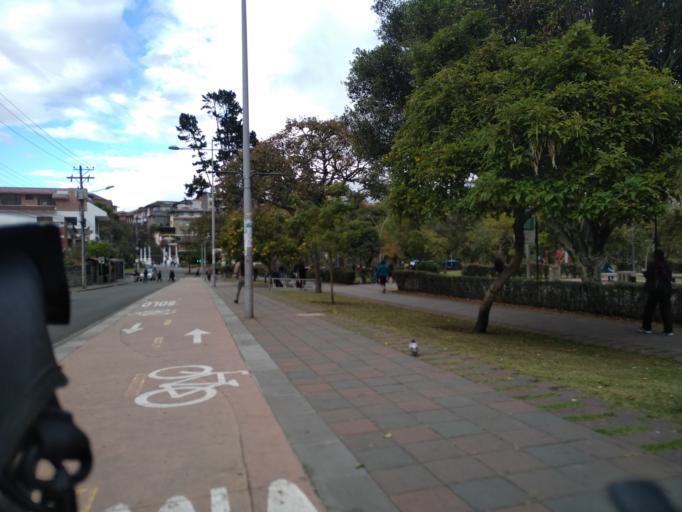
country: EC
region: Azuay
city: Cuenca
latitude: -2.9042
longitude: -79.0041
